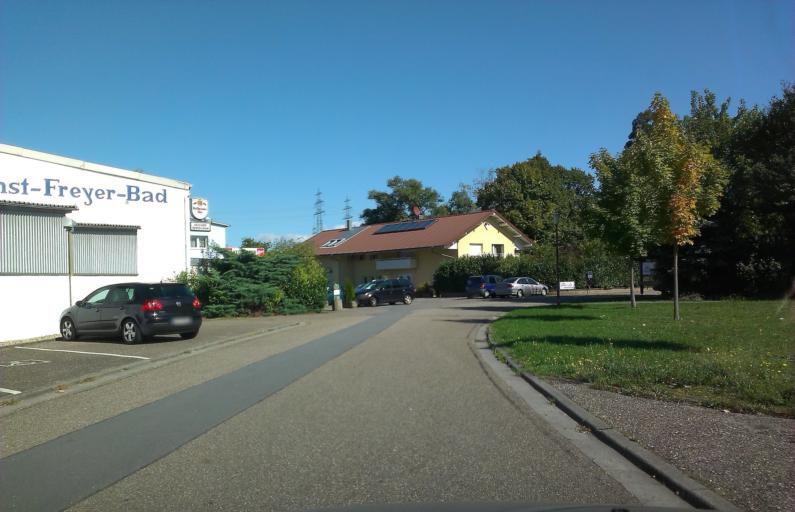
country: DE
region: Baden-Wuerttemberg
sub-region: Karlsruhe Region
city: Philippsburg
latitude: 49.2413
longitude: 8.4599
